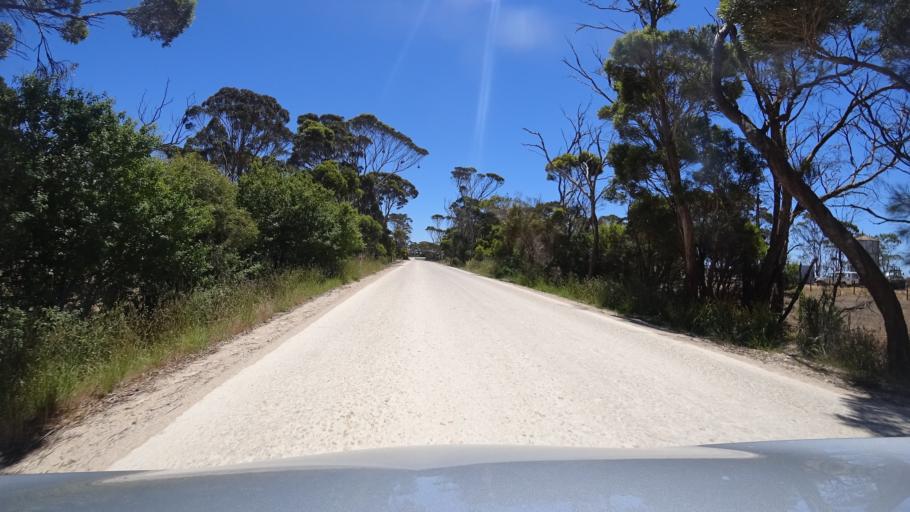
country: AU
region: South Australia
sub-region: Kangaroo Island
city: Kingscote
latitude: -35.7453
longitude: 138.0117
